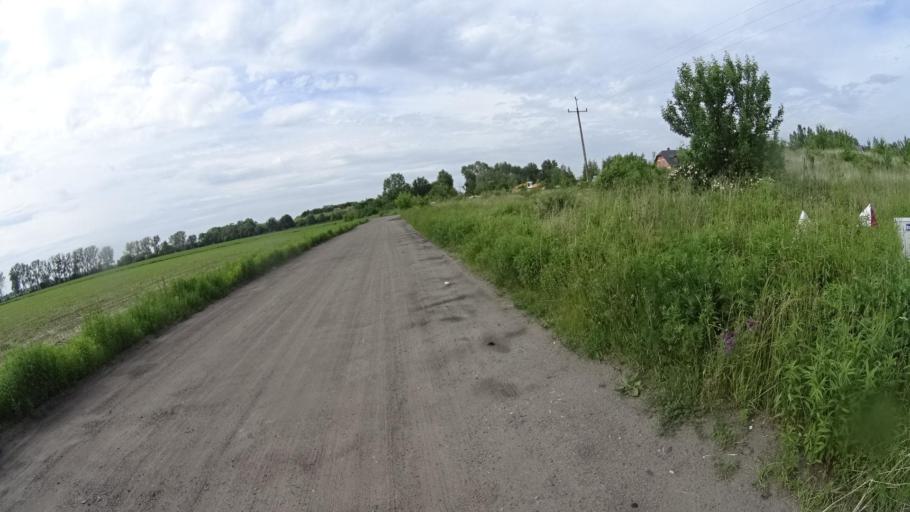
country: PL
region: Masovian Voivodeship
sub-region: Powiat warszawski zachodni
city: Jozefow
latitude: 52.1934
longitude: 20.7424
